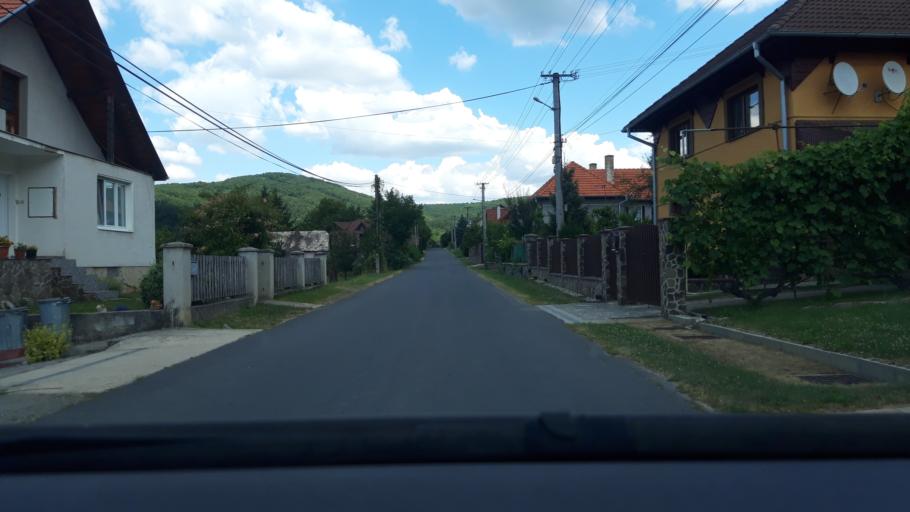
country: HU
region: Nograd
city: Somoskoujfalu
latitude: 48.1804
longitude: 19.8246
